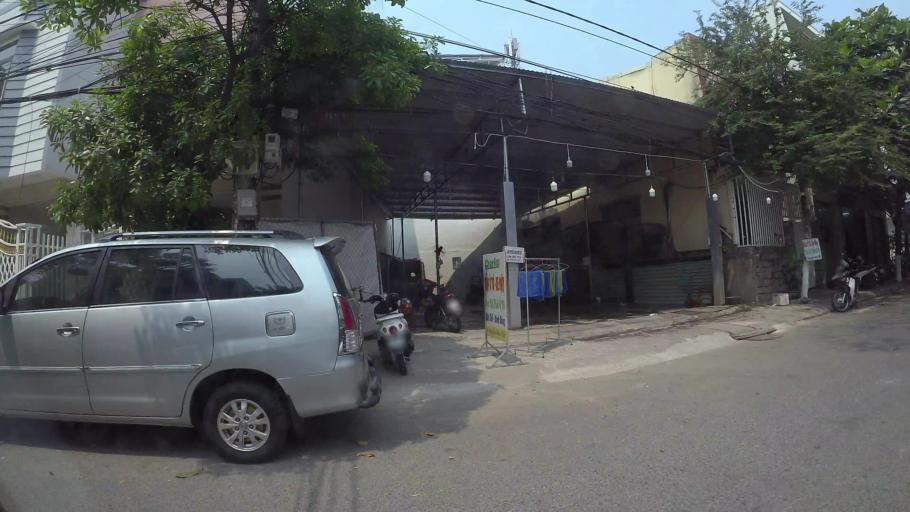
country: VN
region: Da Nang
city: Da Nang
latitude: 16.0806
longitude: 108.2173
